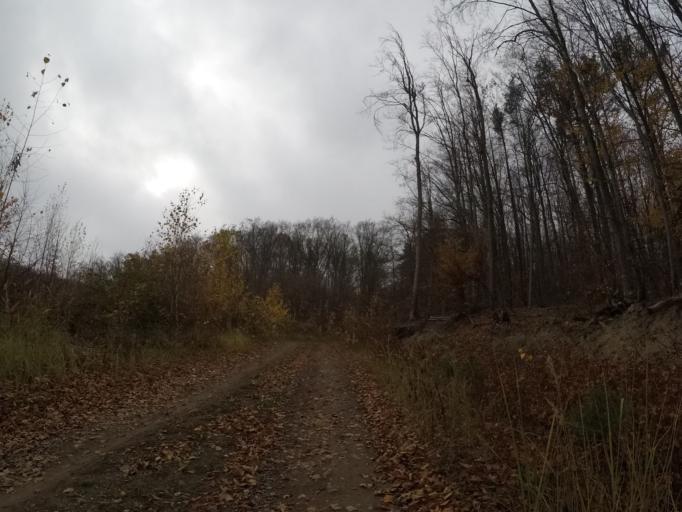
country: SK
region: Presovsky
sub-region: Okres Presov
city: Presov
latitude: 48.8912
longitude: 21.1726
